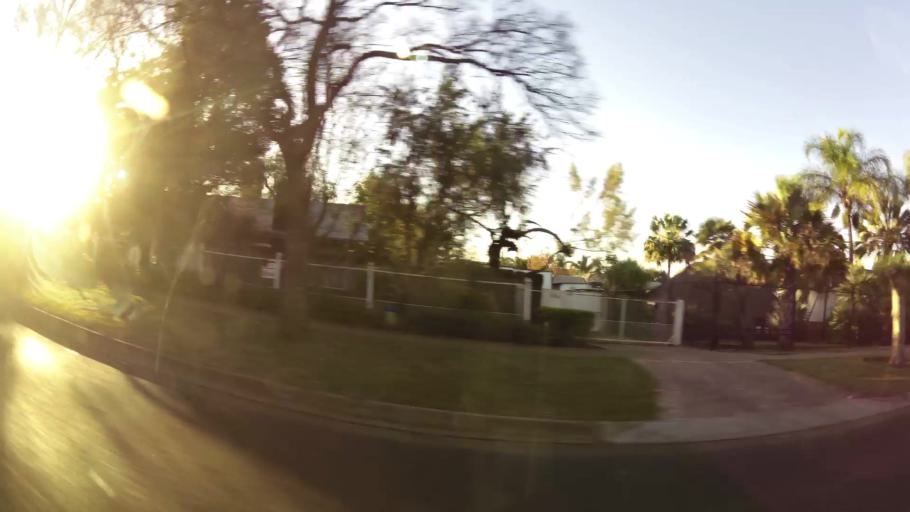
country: ZA
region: Gauteng
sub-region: City of Tshwane Metropolitan Municipality
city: Pretoria
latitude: -25.7151
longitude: 28.2253
